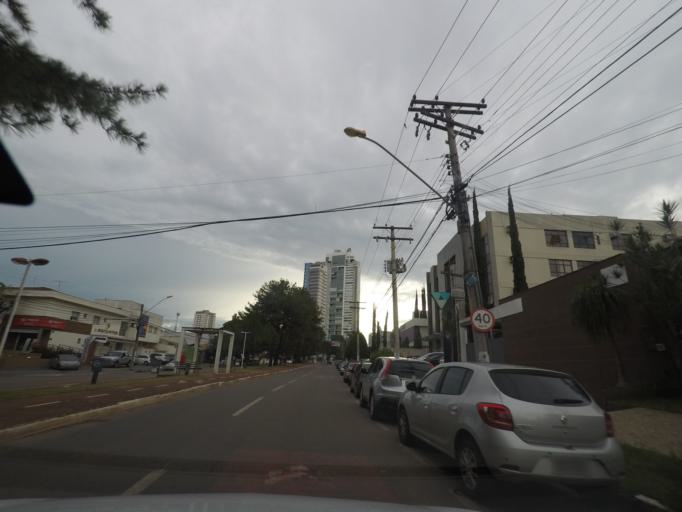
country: BR
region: Goias
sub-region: Goiania
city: Goiania
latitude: -16.7037
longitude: -49.2595
